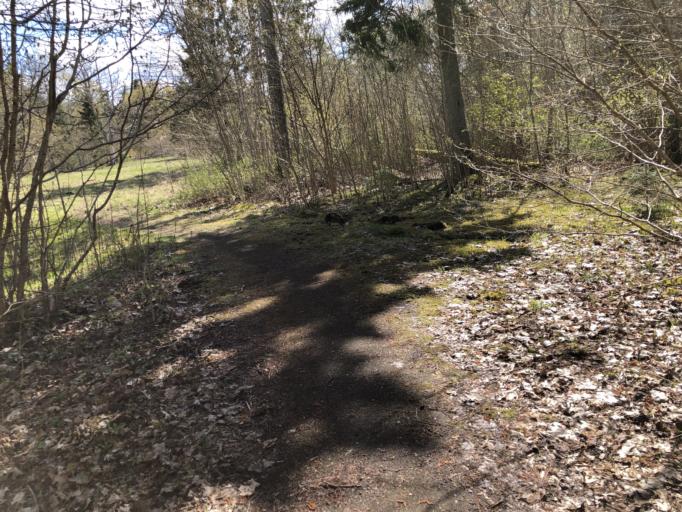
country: EE
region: Harju
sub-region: Harku vald
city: Tabasalu
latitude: 59.4403
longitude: 24.5252
